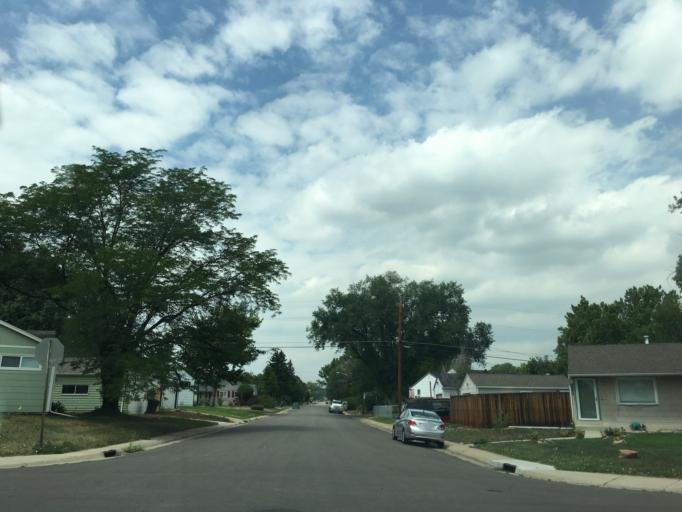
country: US
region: Colorado
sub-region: Arapahoe County
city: Sheridan
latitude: 39.6703
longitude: -105.0319
